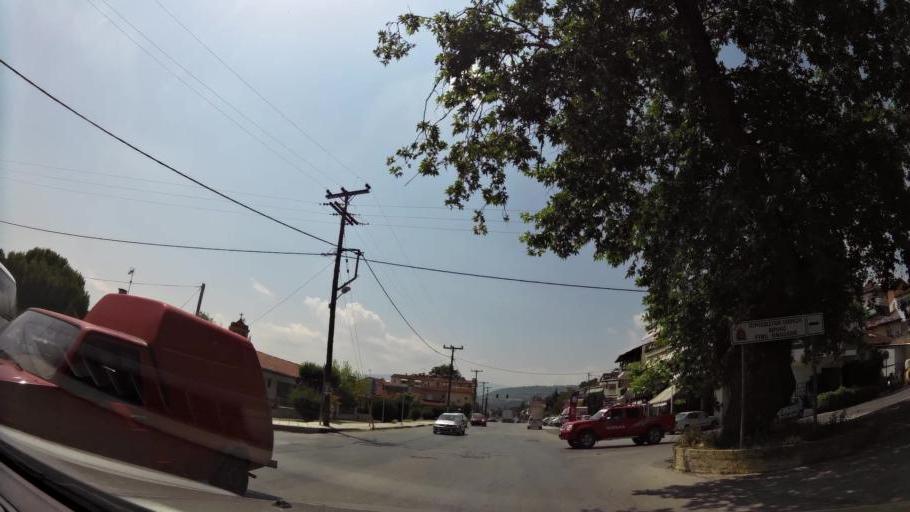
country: GR
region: Central Macedonia
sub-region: Nomos Imathias
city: Veroia
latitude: 40.5312
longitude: 22.2076
